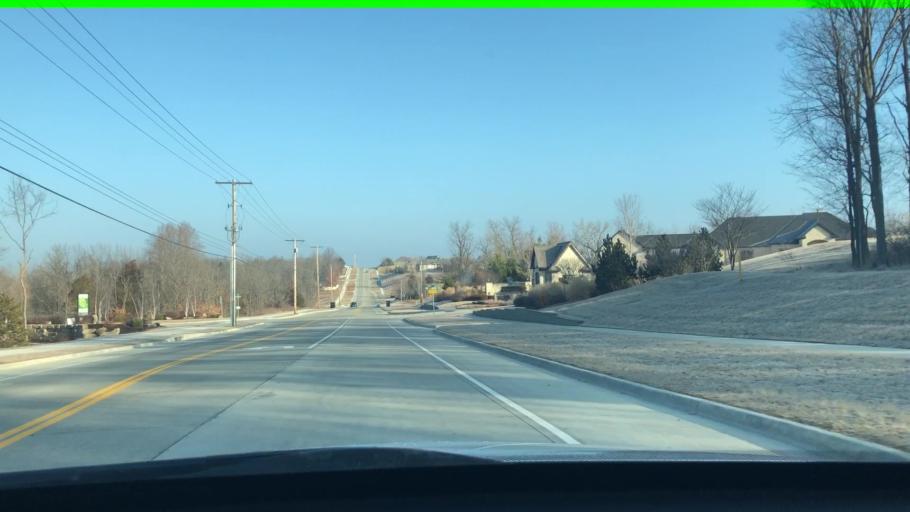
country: US
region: Missouri
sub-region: Boone County
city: Columbia
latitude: 38.9024
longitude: -92.4005
